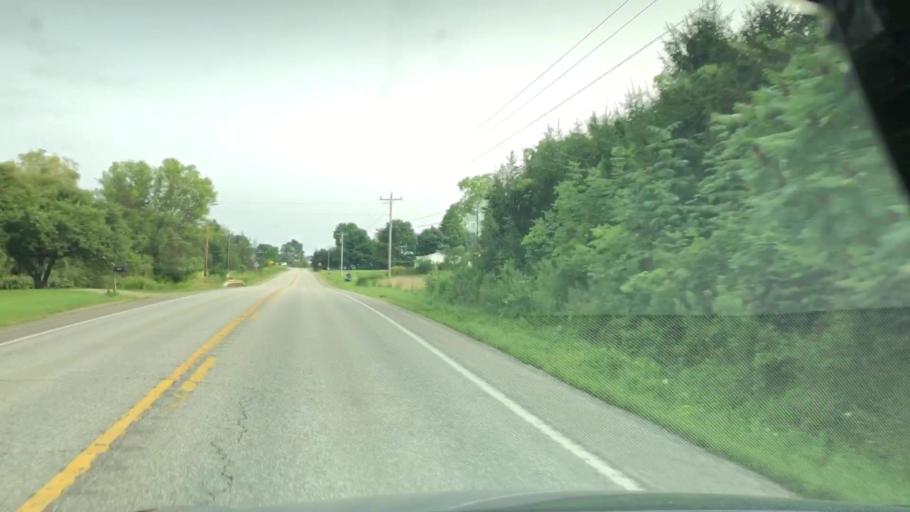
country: US
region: Pennsylvania
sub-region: Erie County
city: Union City
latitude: 41.8758
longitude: -79.8415
